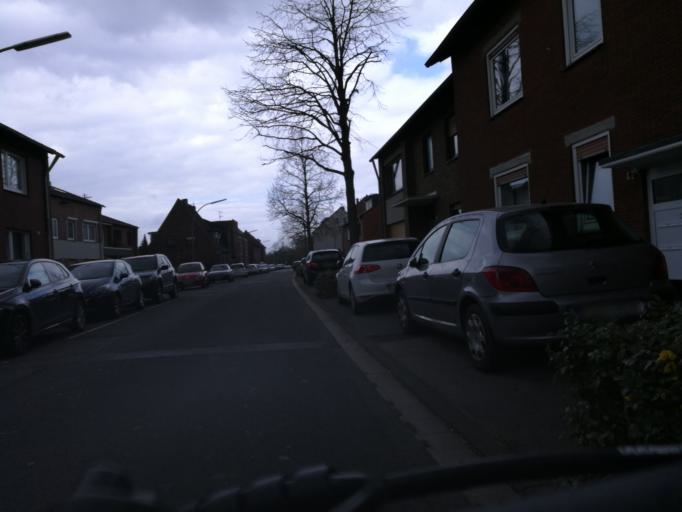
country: DE
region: North Rhine-Westphalia
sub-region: Regierungsbezirk Dusseldorf
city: Dusseldorf
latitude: 51.1650
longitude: 6.7862
